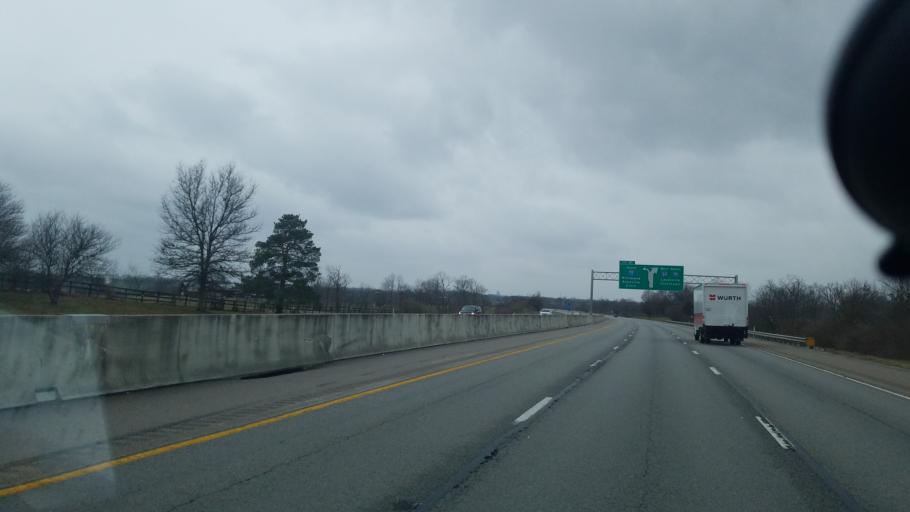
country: US
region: Kentucky
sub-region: Fayette County
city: Lexington-Fayette
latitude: 38.0623
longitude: -84.3887
